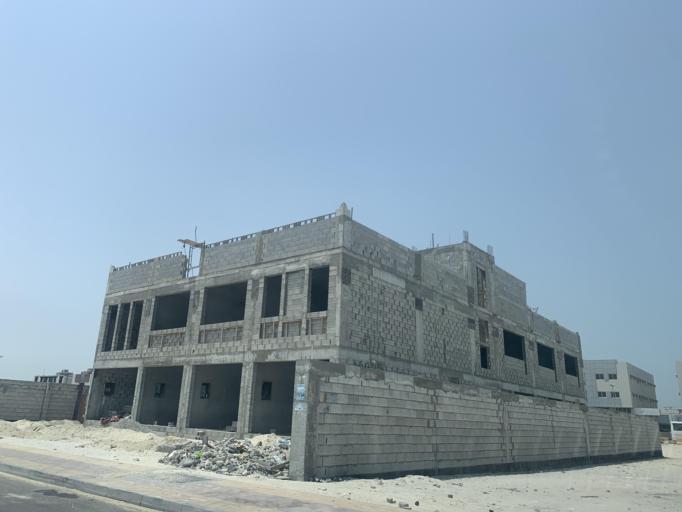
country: BH
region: Muharraq
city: Al Hadd
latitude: 26.2587
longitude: 50.6701
